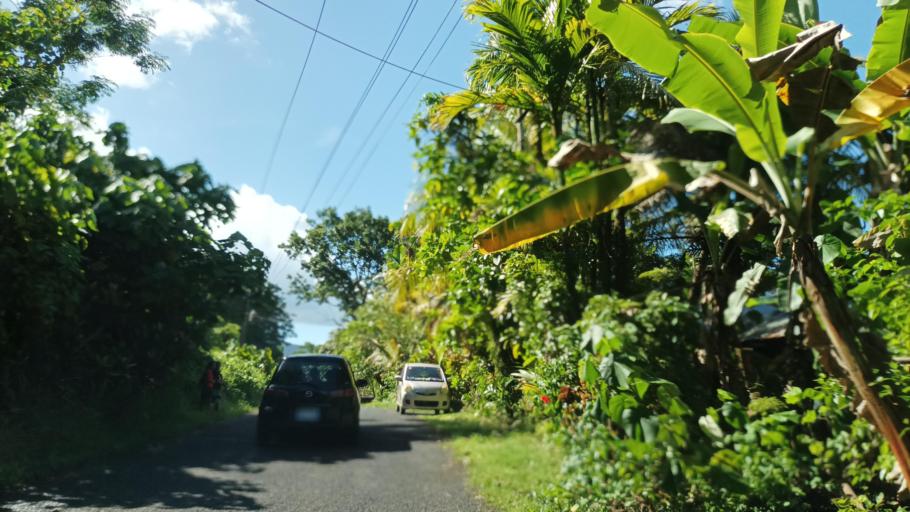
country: FM
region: Pohnpei
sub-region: Madolenihm Municipality
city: Madolenihm Municipality Government
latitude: 6.8637
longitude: 158.2921
